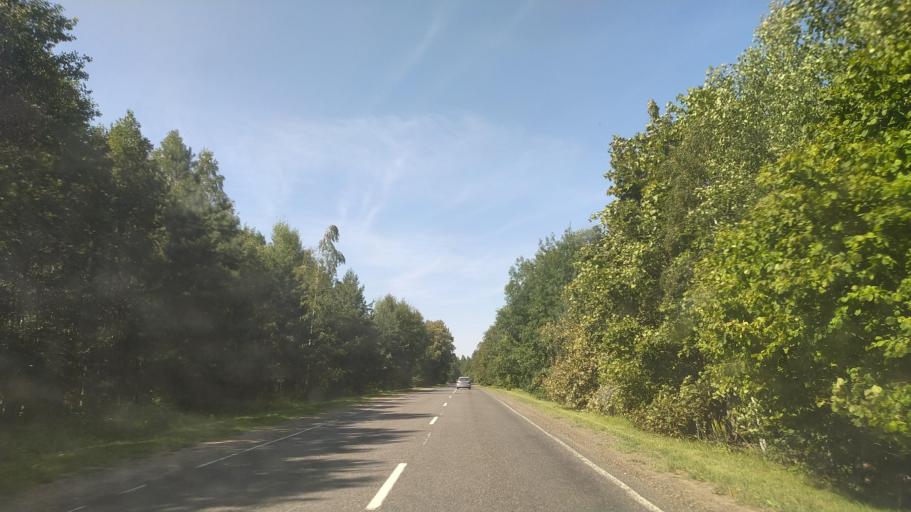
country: BY
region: Brest
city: Byaroza
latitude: 52.4105
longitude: 24.9936
